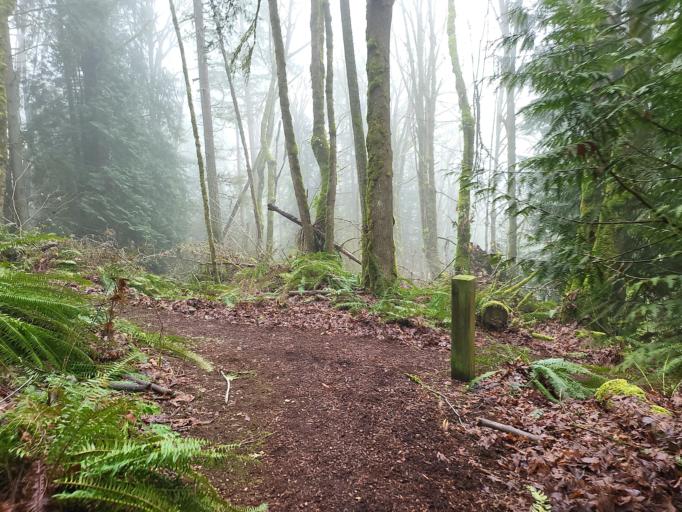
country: US
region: Washington
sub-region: King County
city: Newcastle
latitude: 47.5395
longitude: -122.1282
